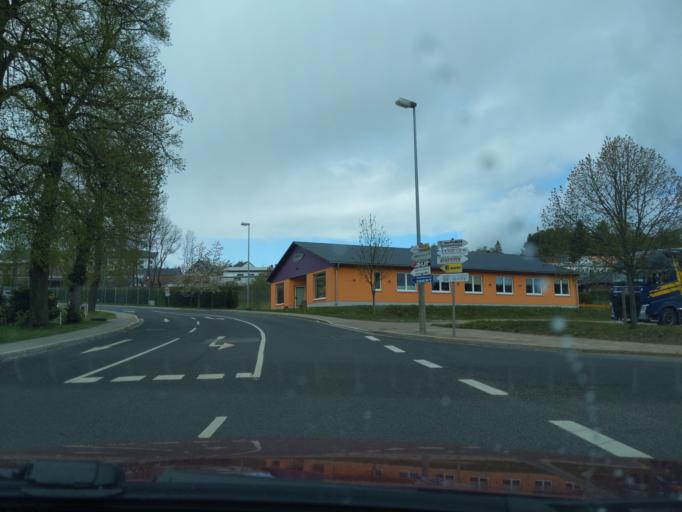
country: DE
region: Saxony
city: Schoenheide
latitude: 50.5052
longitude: 12.5221
